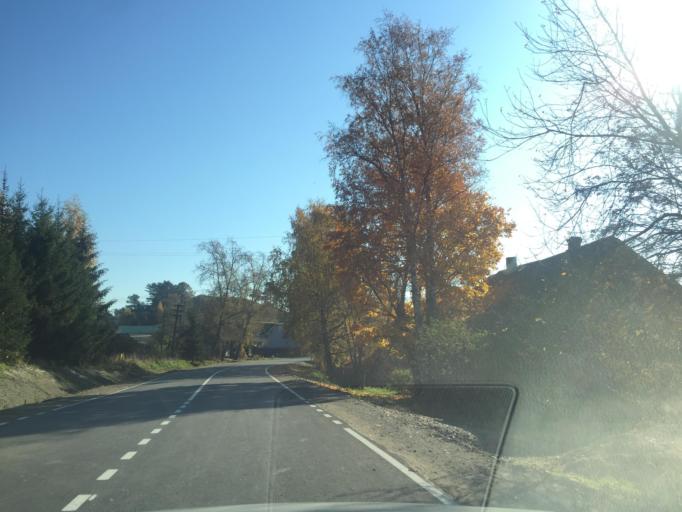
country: RU
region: Leningrad
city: Kuznechnoye
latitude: 61.3020
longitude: 29.8860
